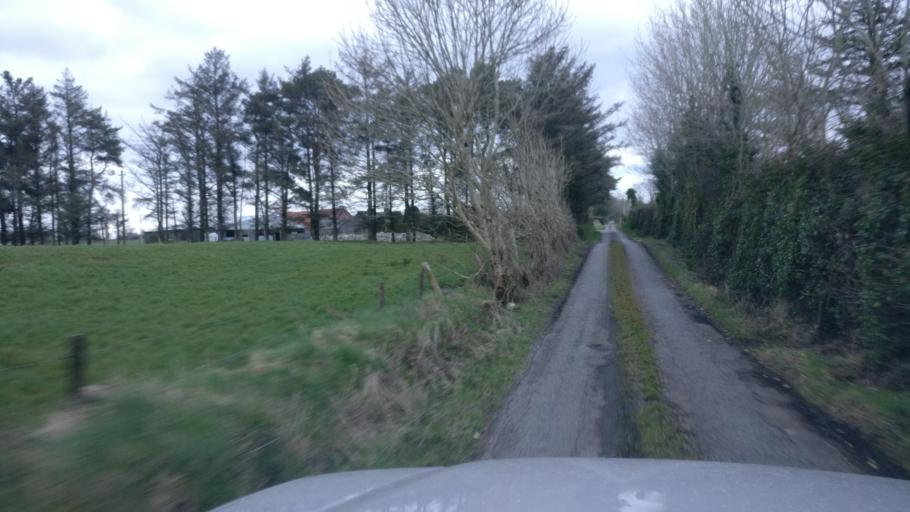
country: IE
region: Connaught
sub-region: County Galway
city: Loughrea
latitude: 53.2614
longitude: -8.4864
